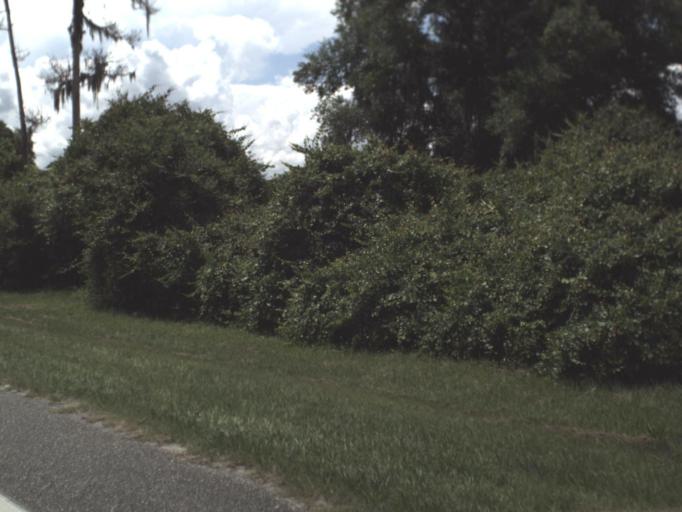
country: US
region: Florida
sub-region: Putnam County
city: Crescent City
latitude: 29.4827
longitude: -81.5578
